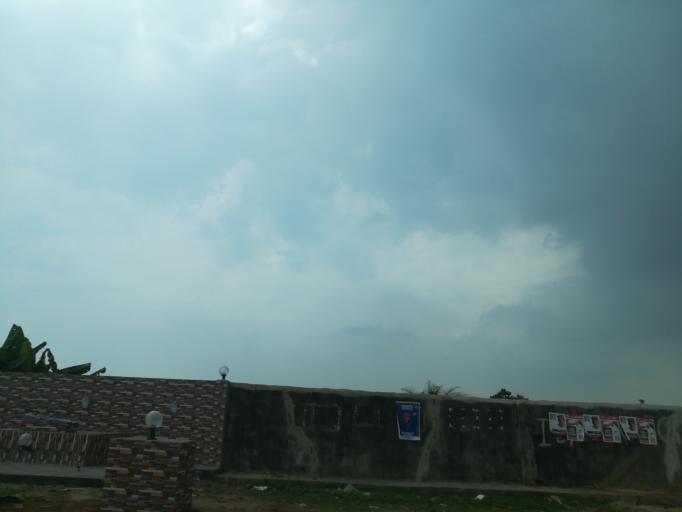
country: NG
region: Lagos
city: Ikorodu
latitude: 6.5818
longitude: 3.5885
